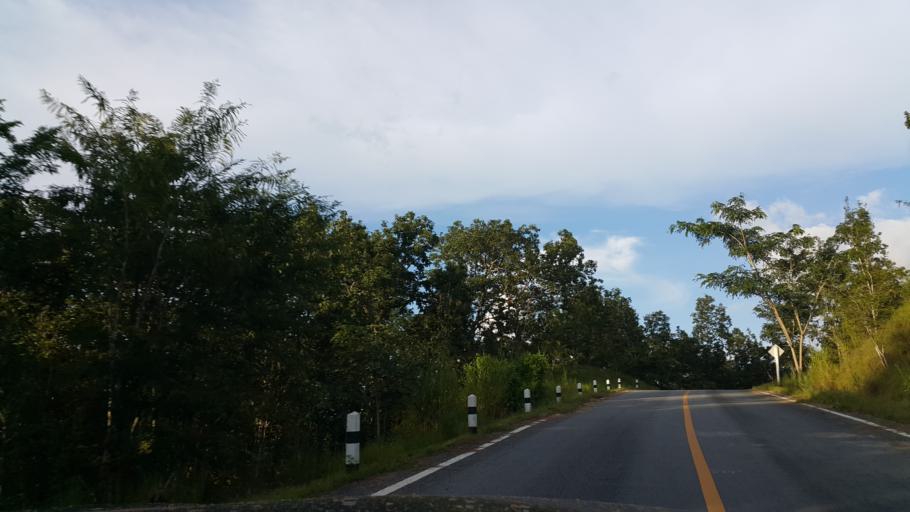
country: TH
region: Mae Hong Son
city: Mae Hi
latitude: 19.1862
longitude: 98.4111
